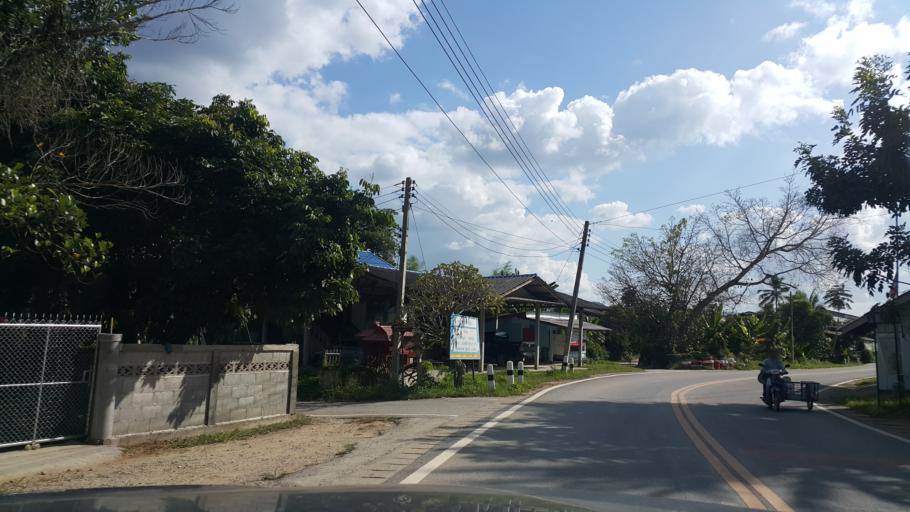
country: TH
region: Lamphun
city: Ban Thi
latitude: 18.6010
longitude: 99.2719
